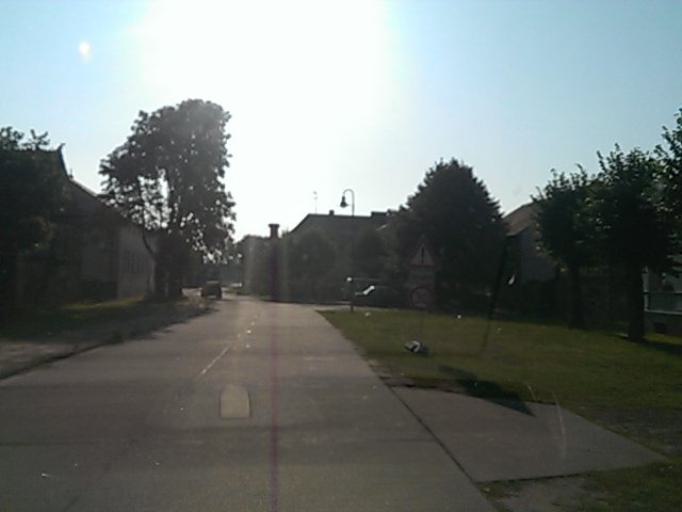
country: DE
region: Brandenburg
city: Michendorf
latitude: 52.2696
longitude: 13.1212
